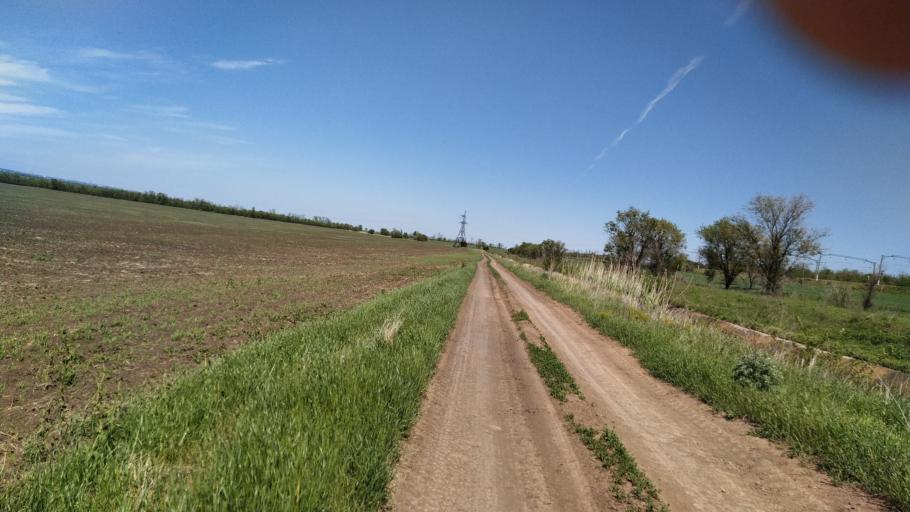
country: RU
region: Rostov
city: Kuleshovka
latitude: 47.0360
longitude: 39.6387
